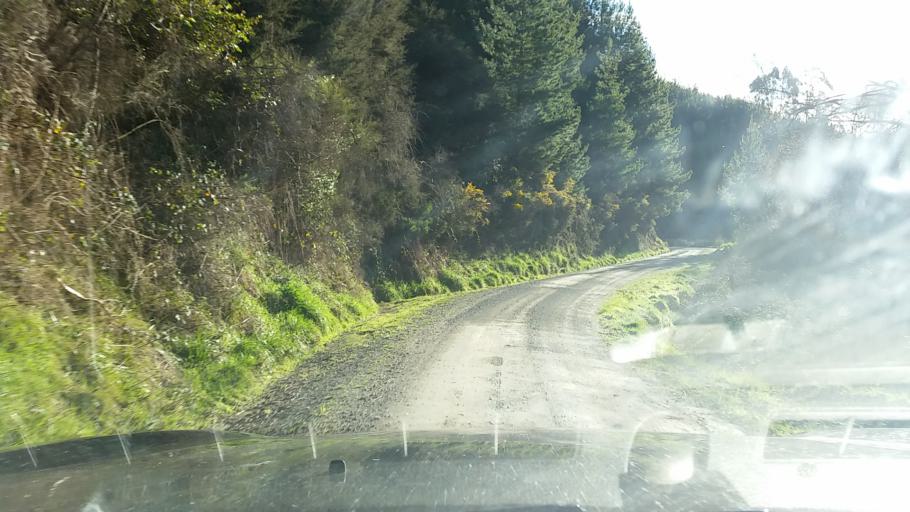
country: NZ
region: Nelson
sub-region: Nelson City
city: Nelson
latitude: -41.5628
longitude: 173.4342
